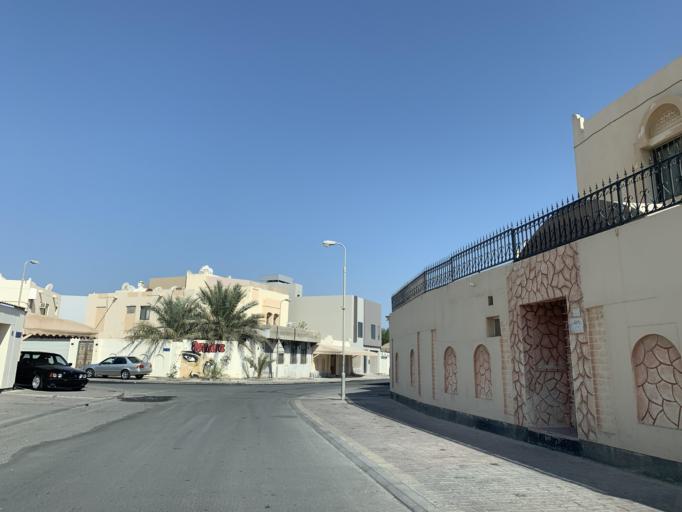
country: BH
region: Central Governorate
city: Madinat Hamad
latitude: 26.1286
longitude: 50.4814
